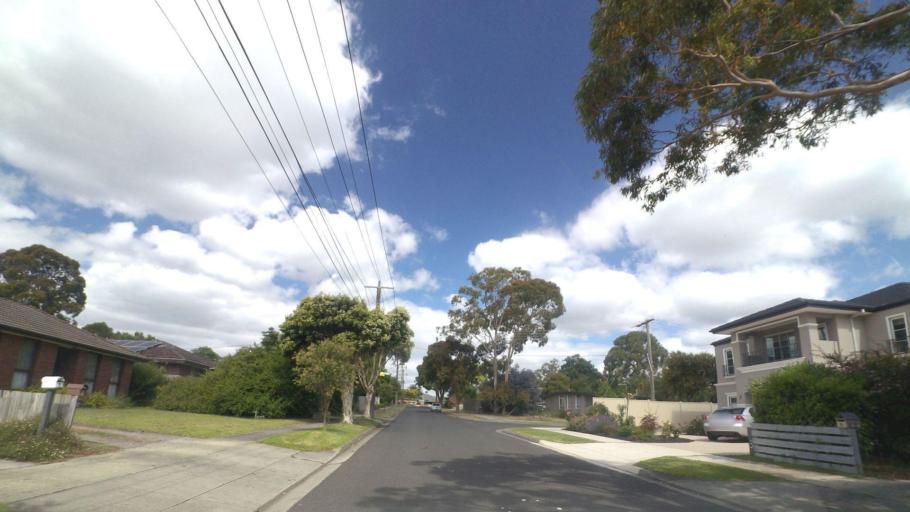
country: AU
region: Victoria
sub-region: Knox
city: Bayswater
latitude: -37.8648
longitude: 145.2587
